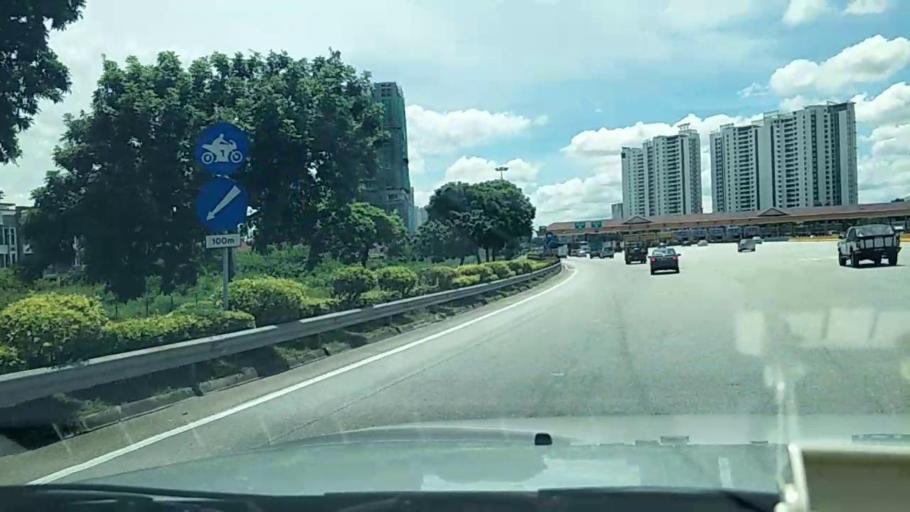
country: MY
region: Selangor
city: Subang Jaya
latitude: 3.0573
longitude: 101.6102
